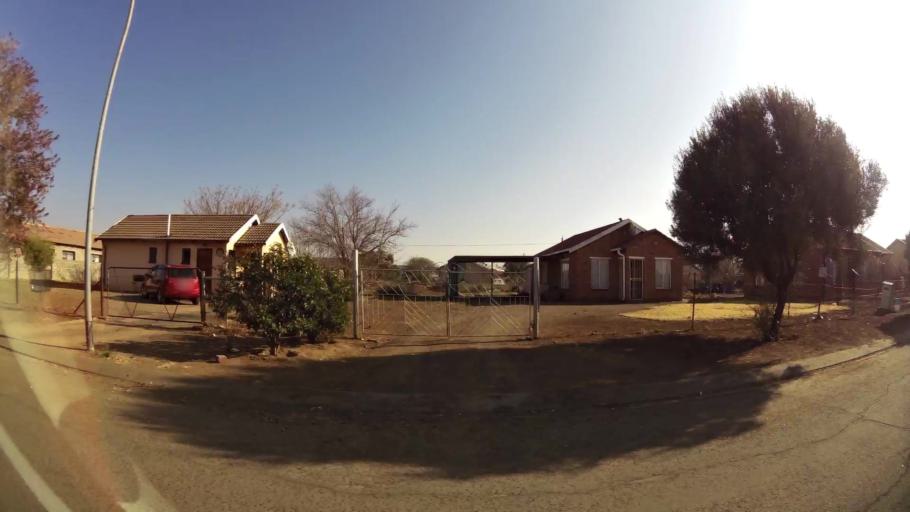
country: ZA
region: Orange Free State
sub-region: Mangaung Metropolitan Municipality
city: Bloemfontein
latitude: -29.1825
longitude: 26.1739
